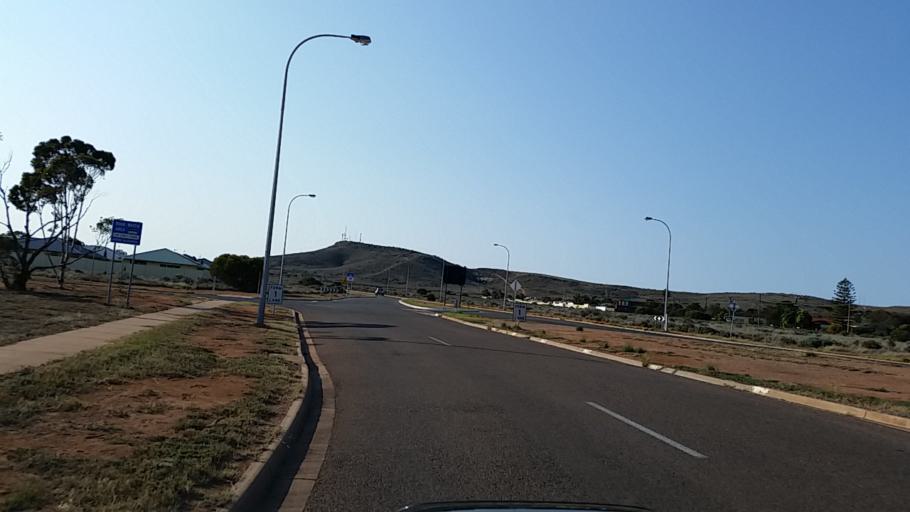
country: AU
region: South Australia
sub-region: Whyalla
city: Whyalla
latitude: -33.0156
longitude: 137.5294
